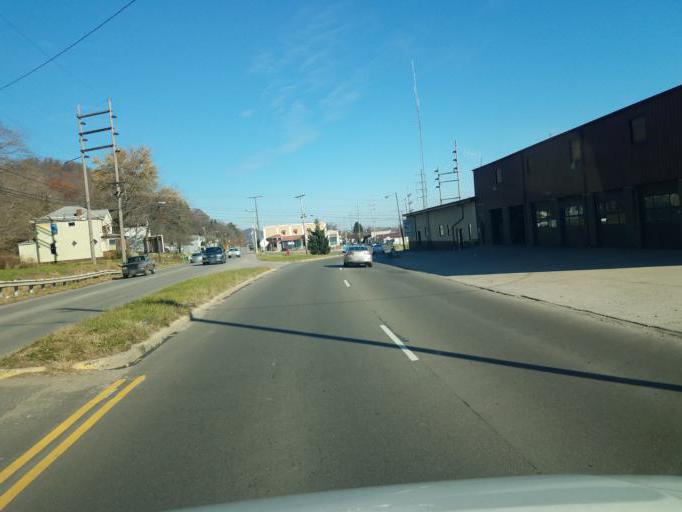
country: US
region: Kentucky
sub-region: Greenup County
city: South Shore
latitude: 38.7415
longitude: -82.9594
